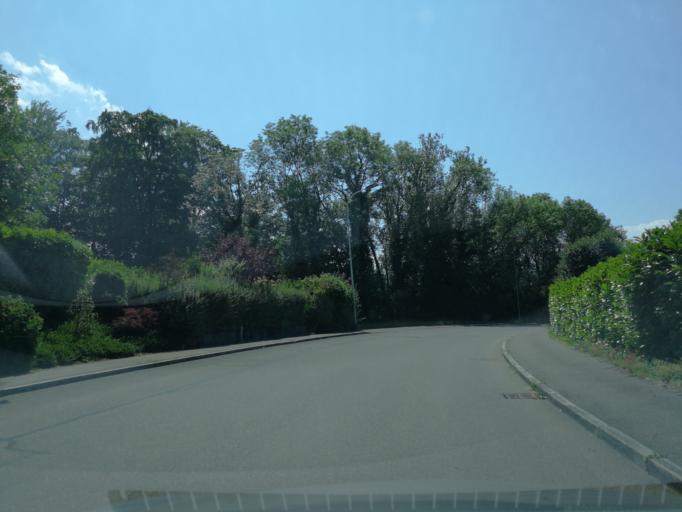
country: CH
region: Zurich
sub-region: Bezirk Meilen
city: Meilen
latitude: 47.2754
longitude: 8.6458
